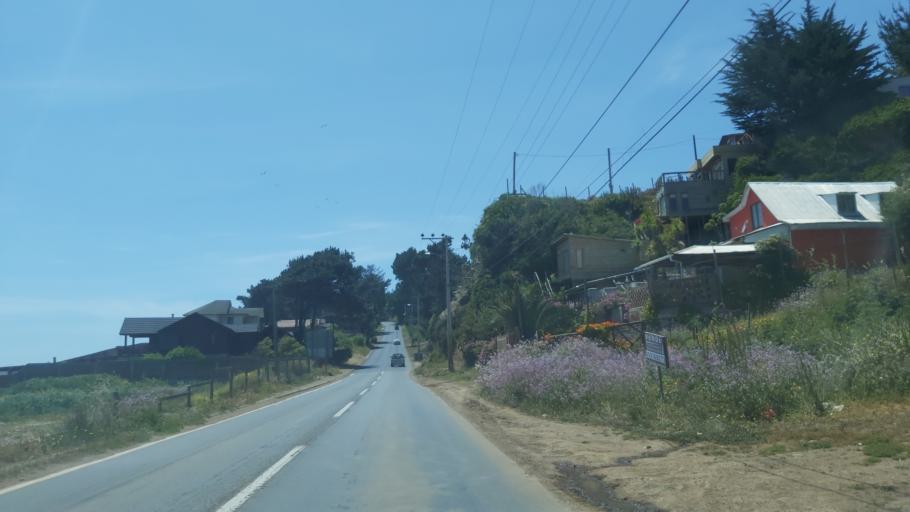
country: CL
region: Maule
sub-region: Provincia de Cauquenes
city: Cauquenes
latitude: -35.8361
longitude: -72.6236
